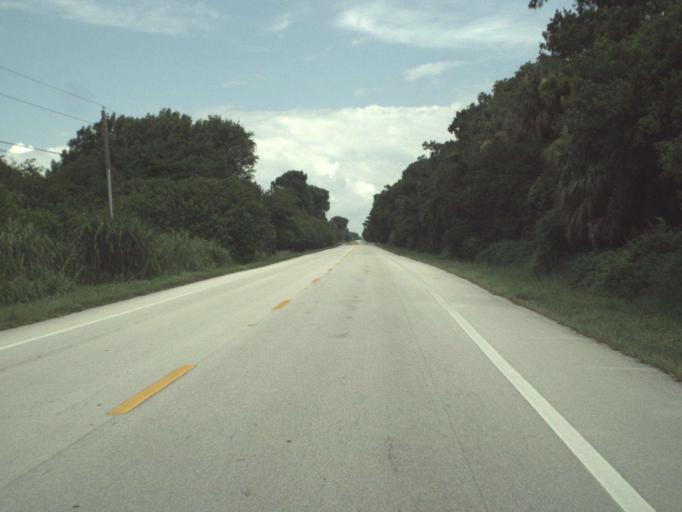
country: US
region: Florida
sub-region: Martin County
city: Indiantown
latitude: 27.0484
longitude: -80.6419
